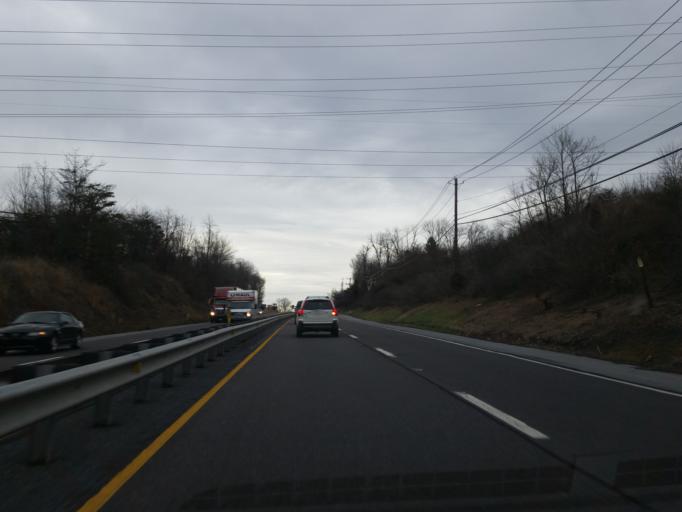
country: US
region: Pennsylvania
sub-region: Dauphin County
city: Linglestown
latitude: 40.3289
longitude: -76.7597
